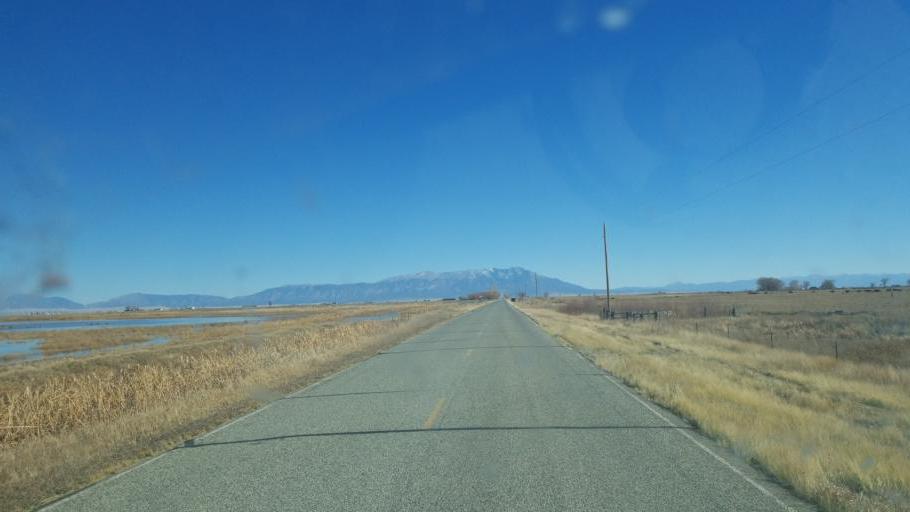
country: US
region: Colorado
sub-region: Rio Grande County
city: Monte Vista
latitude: 37.5744
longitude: -105.9894
